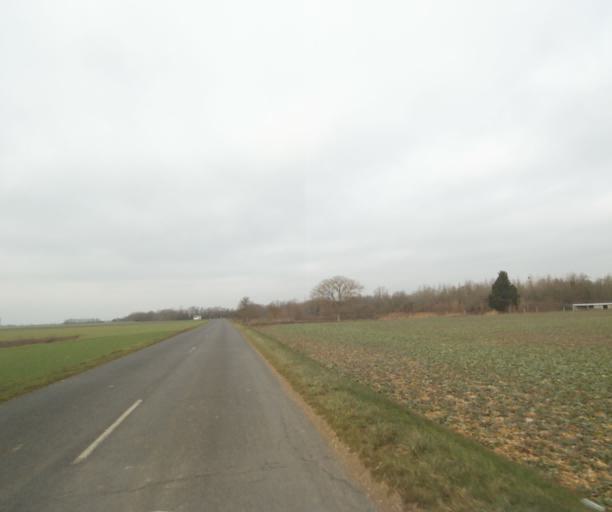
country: FR
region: Champagne-Ardenne
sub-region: Departement de la Haute-Marne
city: Villiers-en-Lieu
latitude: 48.6526
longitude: 4.8009
